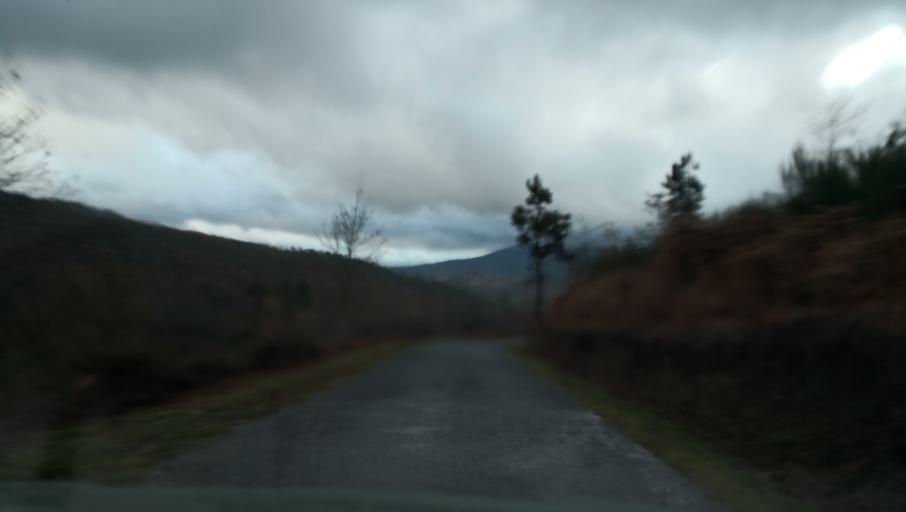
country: PT
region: Vila Real
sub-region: Santa Marta de Penaguiao
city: Santa Marta de Penaguiao
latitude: 41.3101
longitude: -7.8670
